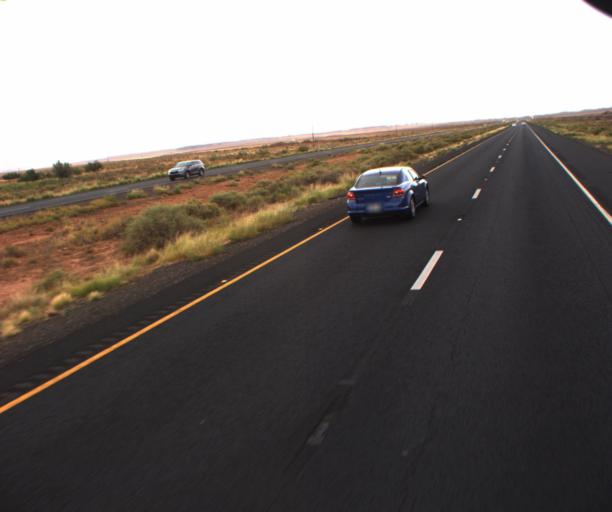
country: US
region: Arizona
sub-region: Coconino County
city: LeChee
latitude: 35.0613
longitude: -110.8149
